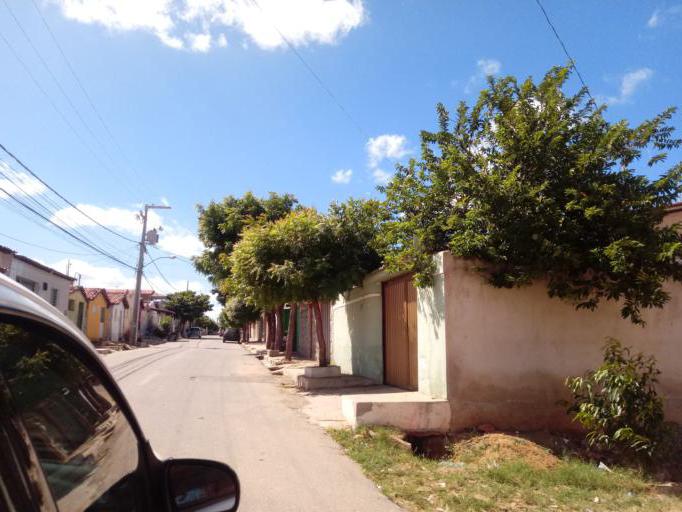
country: BR
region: Paraiba
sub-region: Patos
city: Patos
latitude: -7.0149
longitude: -37.2673
